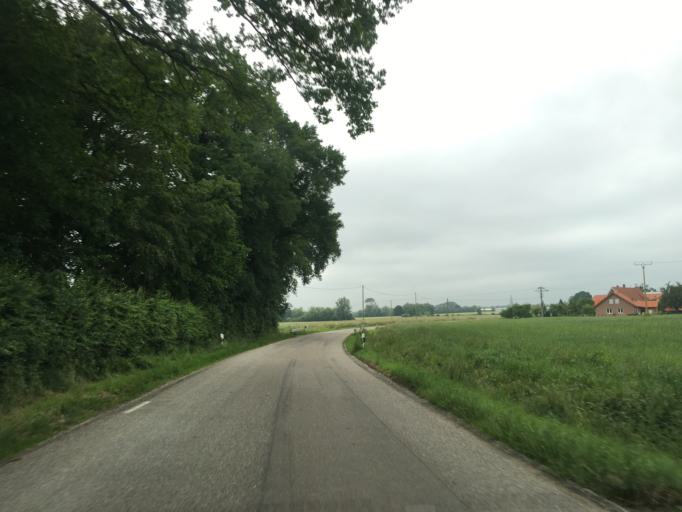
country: DE
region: North Rhine-Westphalia
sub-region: Regierungsbezirk Munster
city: Altenberge
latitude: 52.0229
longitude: 7.4603
